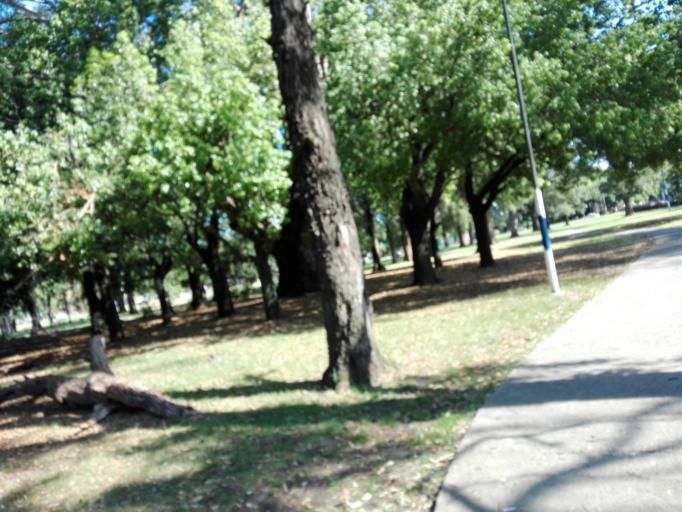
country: AR
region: Buenos Aires
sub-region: Partido de La Plata
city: La Plata
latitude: -34.9335
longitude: -57.9683
